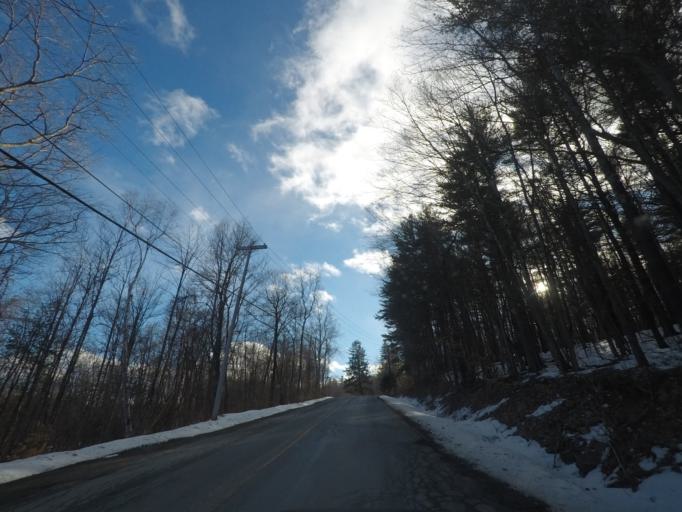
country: US
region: New York
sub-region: Rensselaer County
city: Hoosick Falls
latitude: 42.8211
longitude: -73.3900
